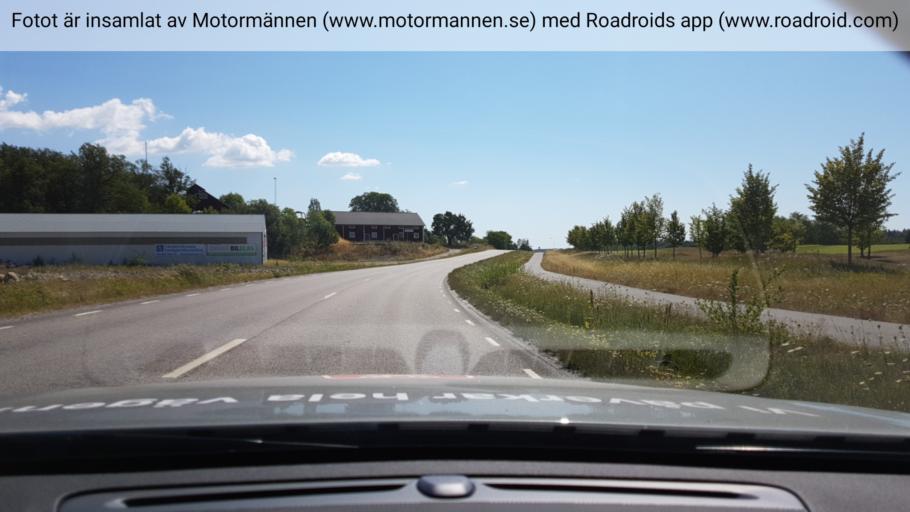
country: SE
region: Stockholm
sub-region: Ekero Kommun
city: Ekeroe
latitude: 59.3190
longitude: 17.7682
